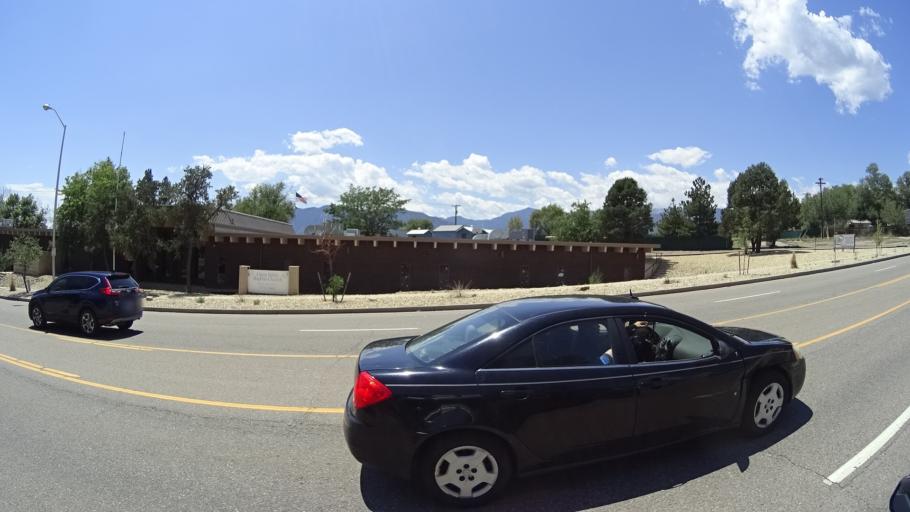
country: US
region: Colorado
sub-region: El Paso County
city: Colorado Springs
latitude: 38.8205
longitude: -104.7933
